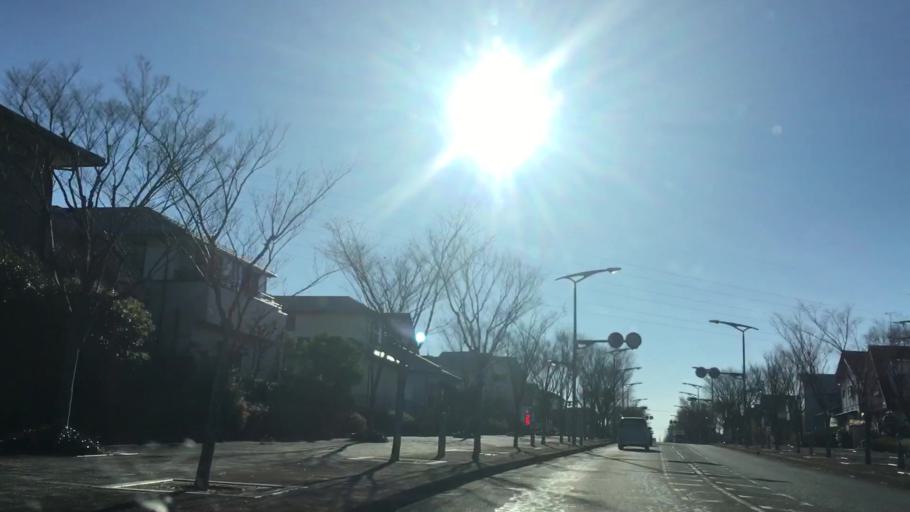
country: JP
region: Shizuoka
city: Hamakita
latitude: 34.8162
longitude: 137.7408
